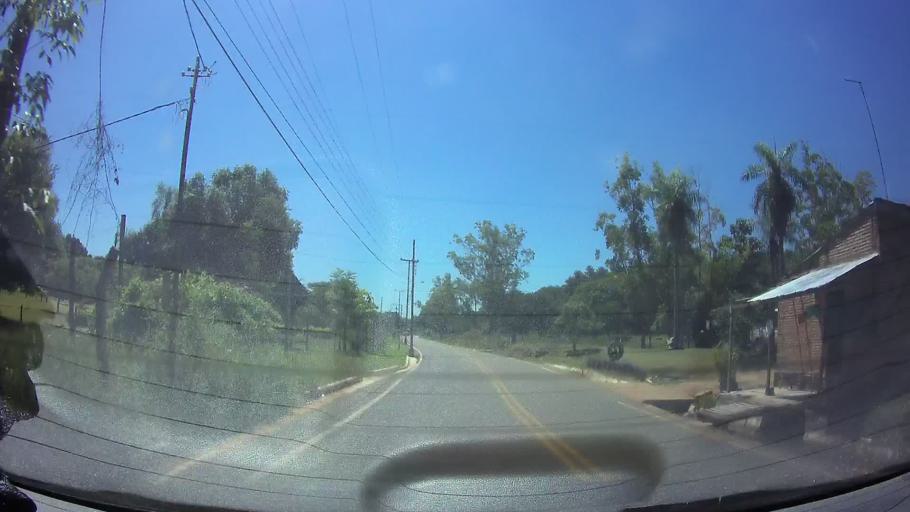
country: PY
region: Central
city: Aregua
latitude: -25.2647
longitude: -57.4336
